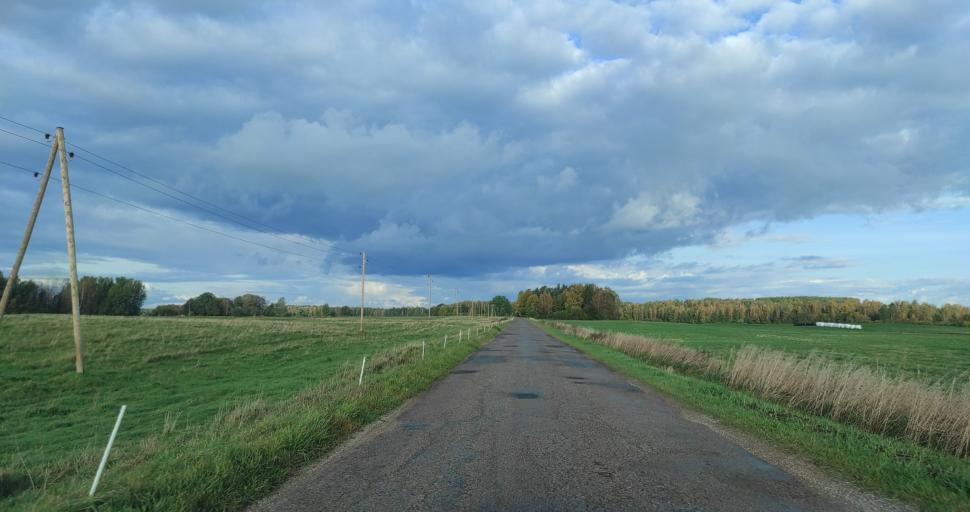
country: LV
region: Aizpute
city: Aizpute
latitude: 56.7873
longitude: 21.7414
